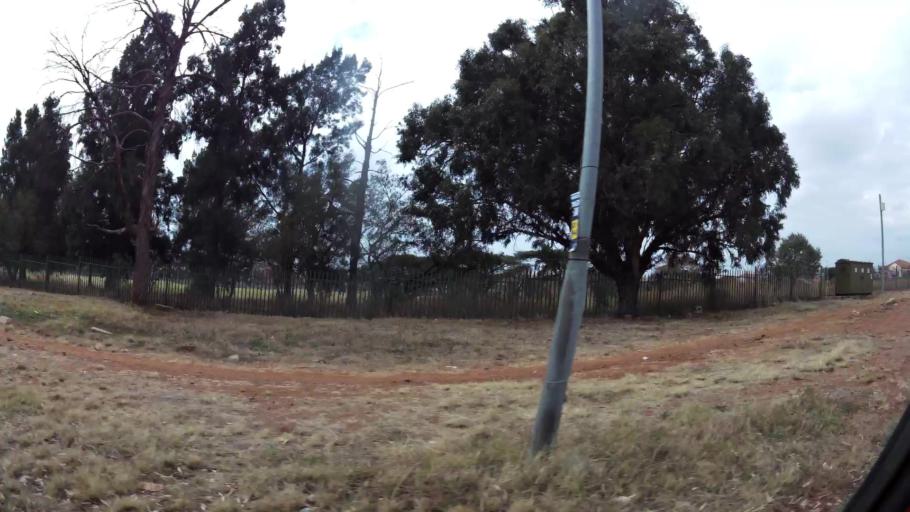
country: ZA
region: Gauteng
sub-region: West Rand District Municipality
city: Muldersdriseloop
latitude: -26.0887
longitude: 27.8687
